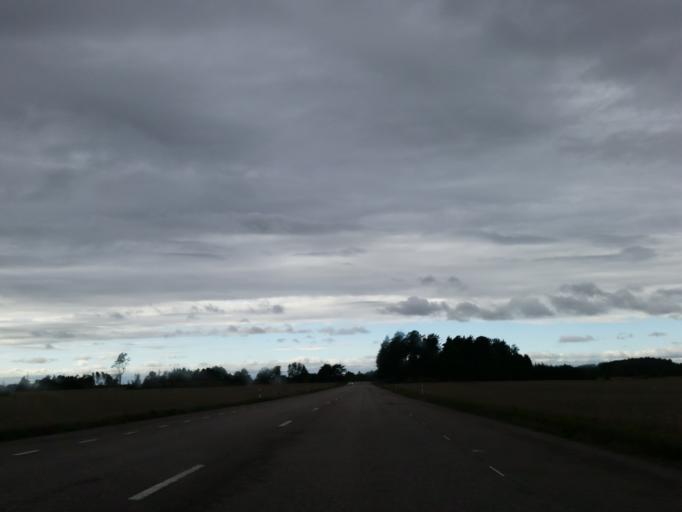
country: SE
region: Uppsala
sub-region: Enkopings Kommun
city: Orsundsbro
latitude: 59.6544
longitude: 17.3567
